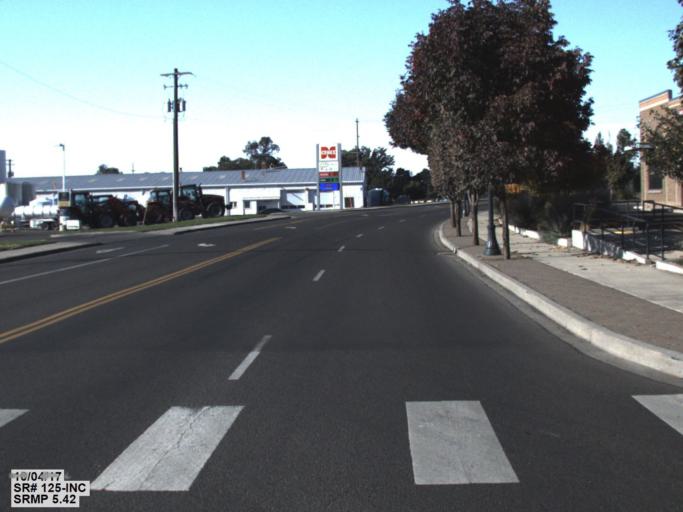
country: US
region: Washington
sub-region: Walla Walla County
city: Walla Walla
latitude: 46.0641
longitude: -118.3493
